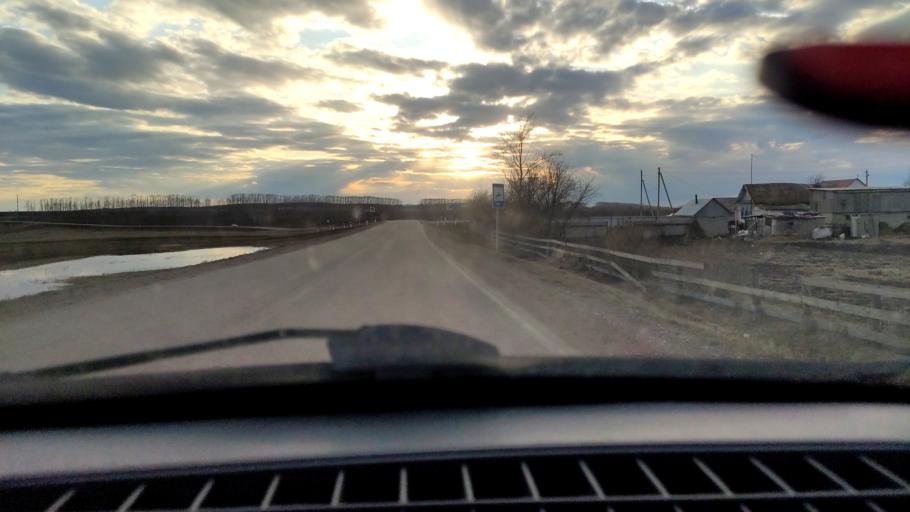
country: RU
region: Bashkortostan
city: Tolbazy
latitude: 53.9885
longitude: 55.8095
